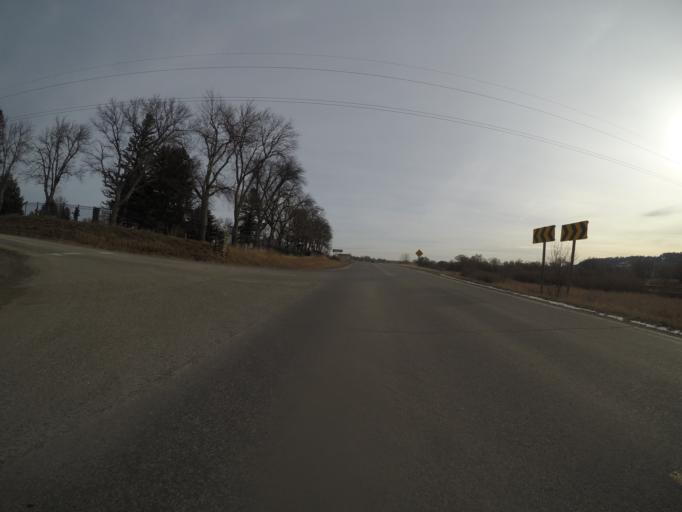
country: US
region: Montana
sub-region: Stillwater County
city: Columbus
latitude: 45.6413
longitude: -109.2745
